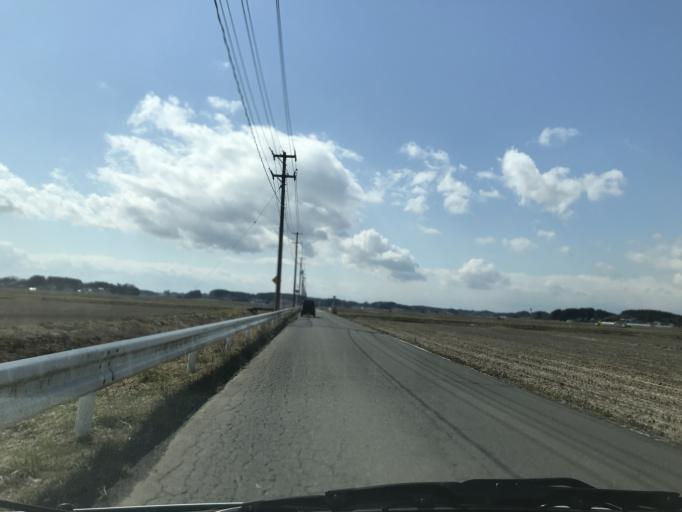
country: JP
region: Miyagi
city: Wakuya
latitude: 38.6828
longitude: 141.1637
